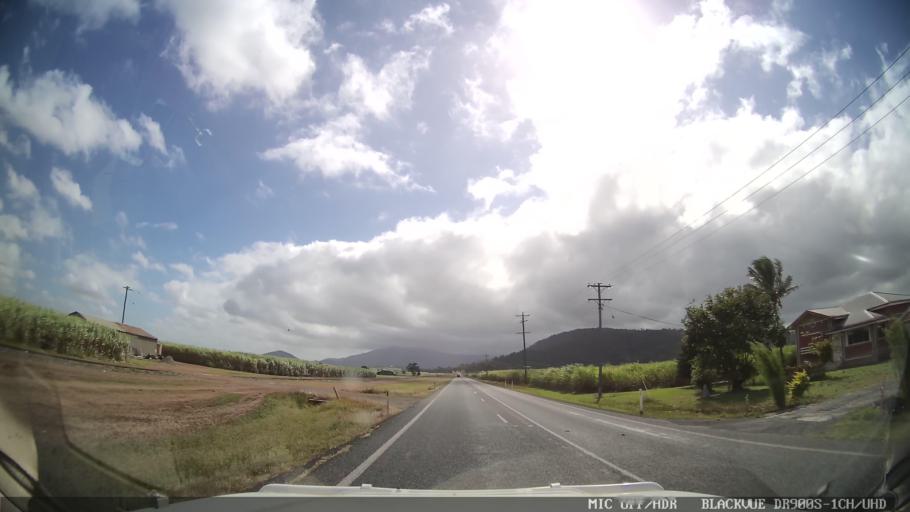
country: AU
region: Queensland
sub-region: Whitsunday
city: Red Hill
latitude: -20.3434
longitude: 148.5528
